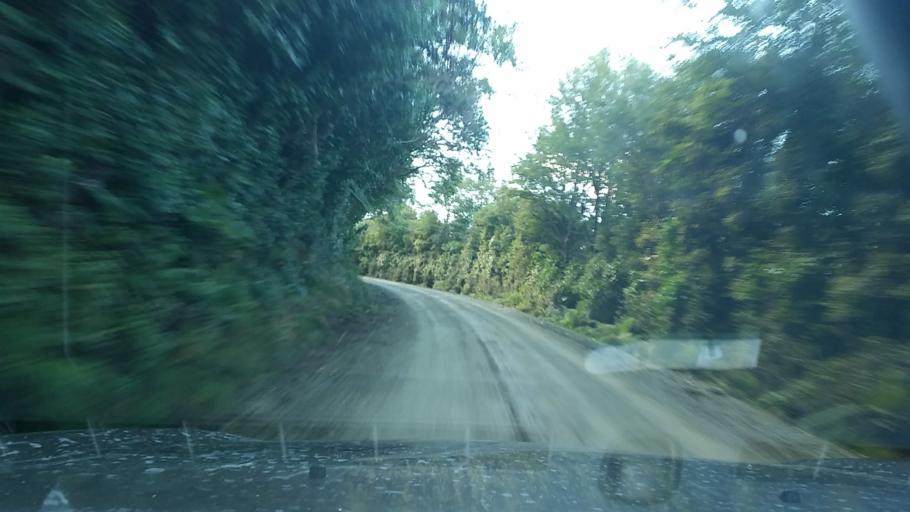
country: NZ
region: Marlborough
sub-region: Marlborough District
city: Picton
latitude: -41.0971
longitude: 174.1355
